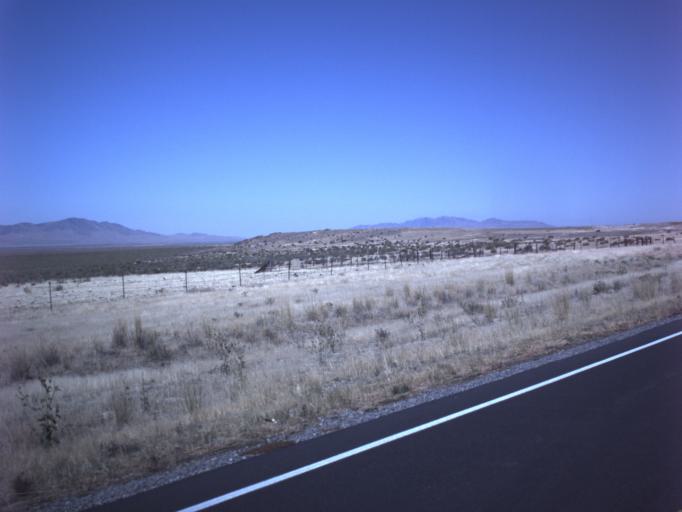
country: US
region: Utah
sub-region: Tooele County
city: Grantsville
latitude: 40.5631
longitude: -112.7342
